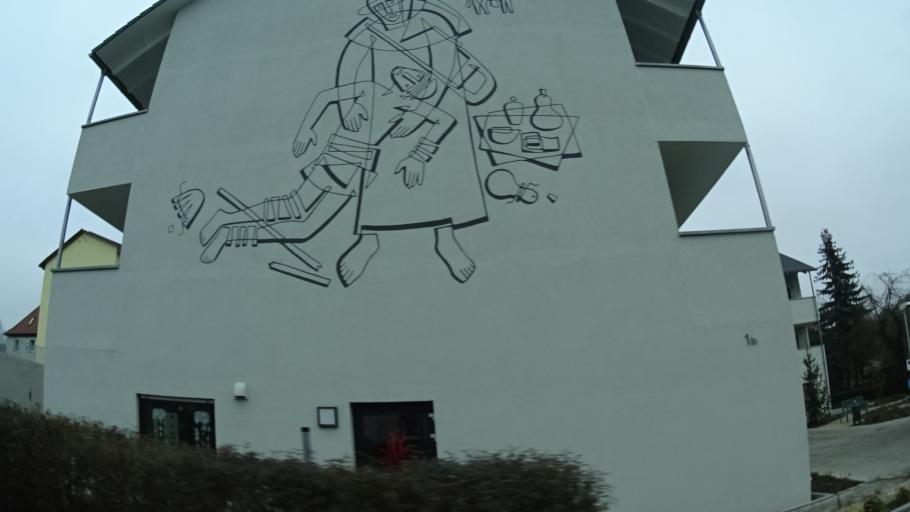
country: DE
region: Baden-Wuerttemberg
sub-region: Regierungsbezirk Stuttgart
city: Boxberg
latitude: 49.4803
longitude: 9.6368
